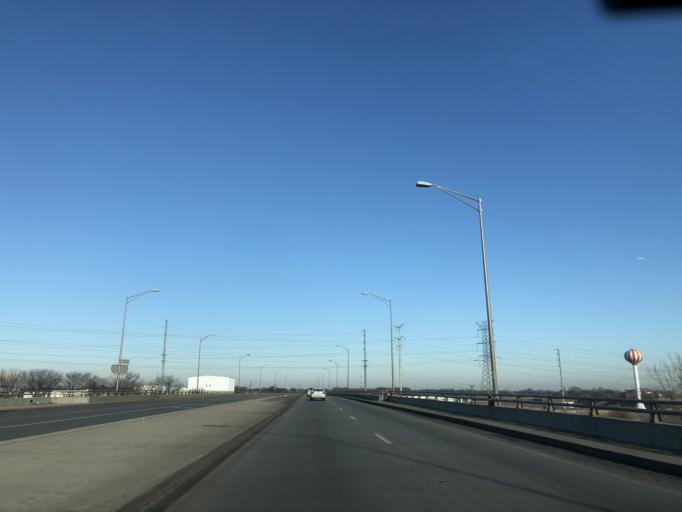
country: US
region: Illinois
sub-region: Cook County
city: Stickney
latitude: 41.8123
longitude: -87.7628
